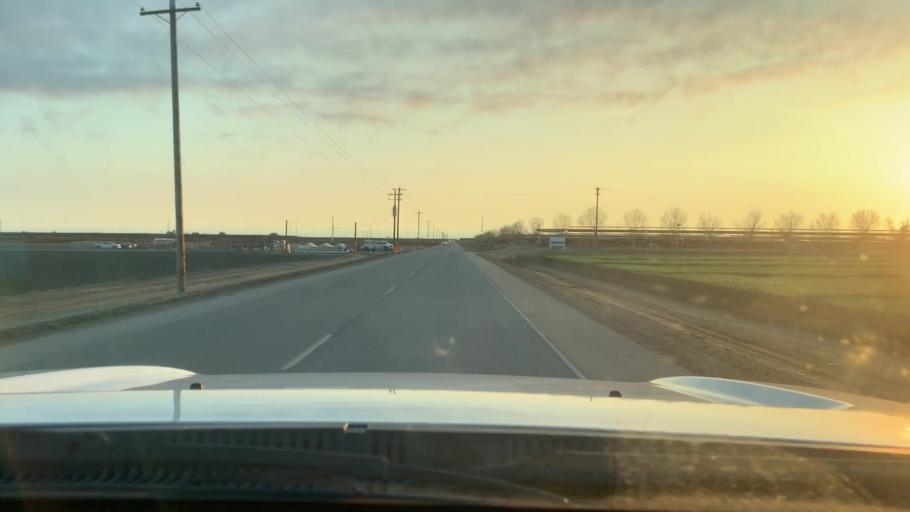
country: US
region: California
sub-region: Kern County
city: Buttonwillow
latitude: 35.5005
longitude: -119.4587
